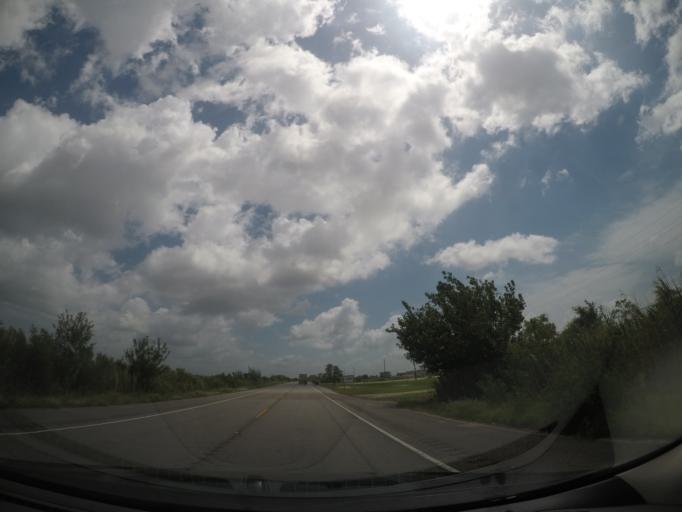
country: US
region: Louisiana
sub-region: Saint Tammany Parish
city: Eden Isle
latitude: 30.1453
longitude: -89.7467
